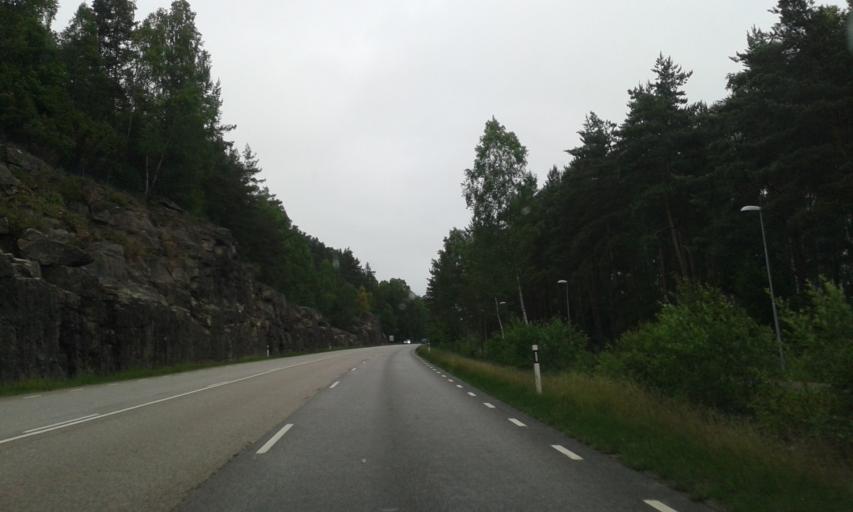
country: SE
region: Vaestra Goetaland
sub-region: Partille Kommun
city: Partille
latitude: 57.7468
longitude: 12.0781
